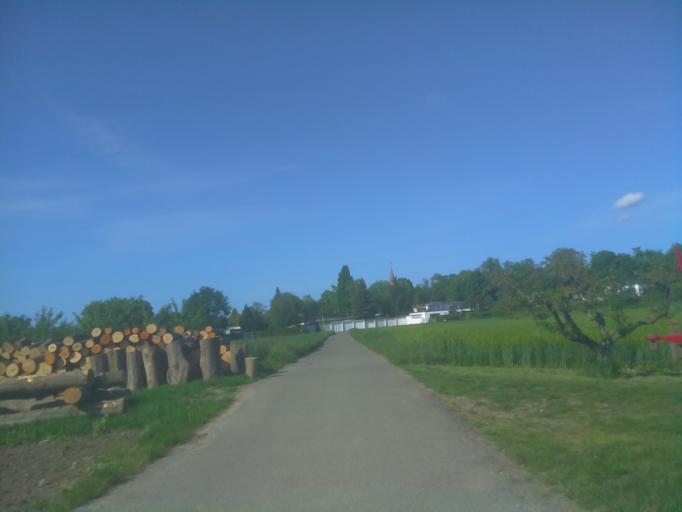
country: DE
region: Baden-Wuerttemberg
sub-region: Karlsruhe Region
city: Edingen-Neckarhausen
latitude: 49.4615
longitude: 8.5964
